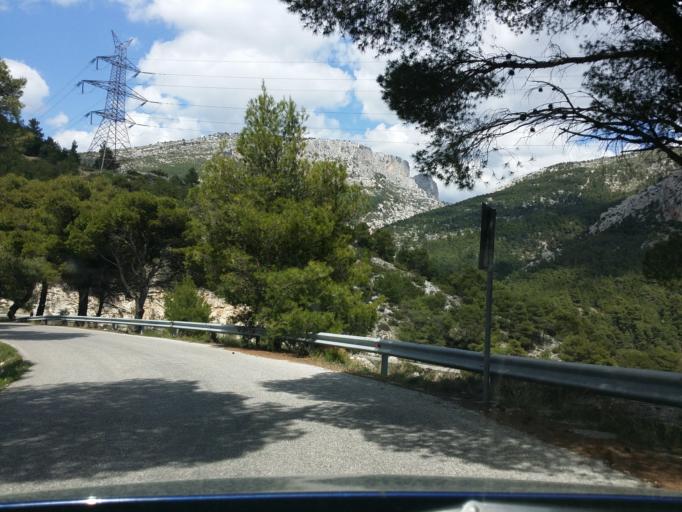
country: GR
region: Attica
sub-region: Nomarchia Dytikis Attikis
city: Fyli
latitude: 38.1204
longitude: 23.6567
